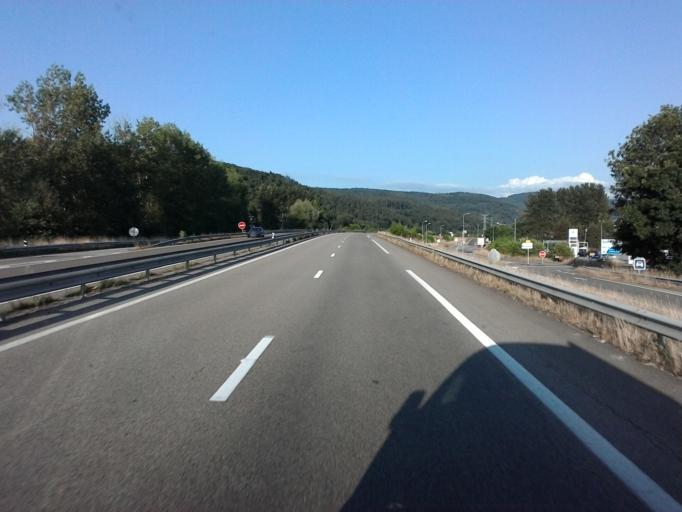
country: FR
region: Lorraine
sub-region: Departement des Vosges
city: Pouxeux
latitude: 48.1102
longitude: 6.5703
